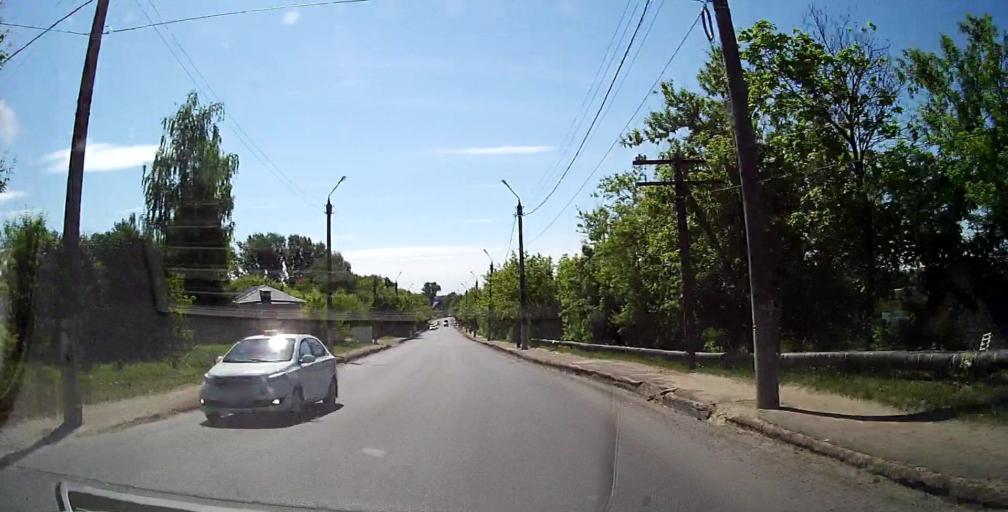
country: RU
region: Lipetsk
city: Dankov
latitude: 53.2435
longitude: 39.1423
